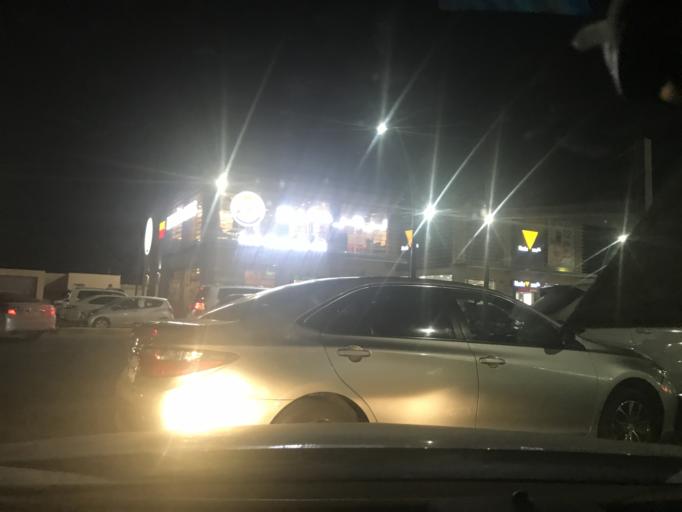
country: SA
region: Ar Riyad
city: Riyadh
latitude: 24.8472
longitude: 46.7336
